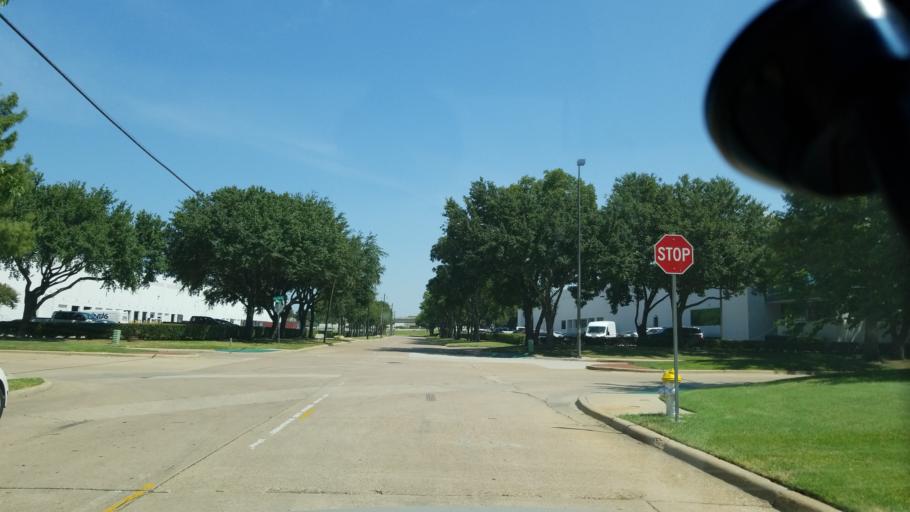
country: US
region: Texas
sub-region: Dallas County
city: Farmers Branch
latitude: 32.9038
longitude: -96.9024
